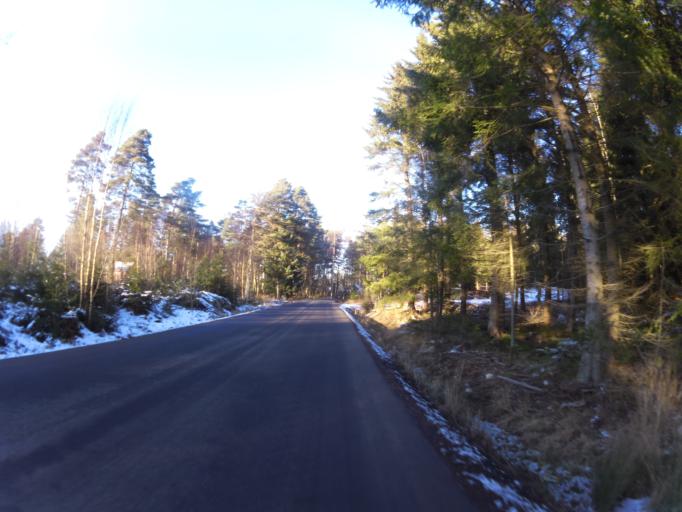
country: NO
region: Ostfold
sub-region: Fredrikstad
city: Lervik
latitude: 59.2604
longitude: 10.8064
